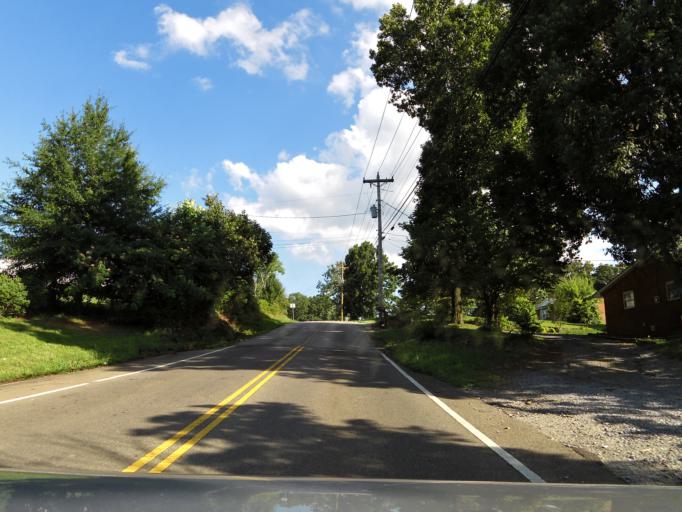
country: US
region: Tennessee
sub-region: Blount County
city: Maryville
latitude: 35.7140
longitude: -84.0151
